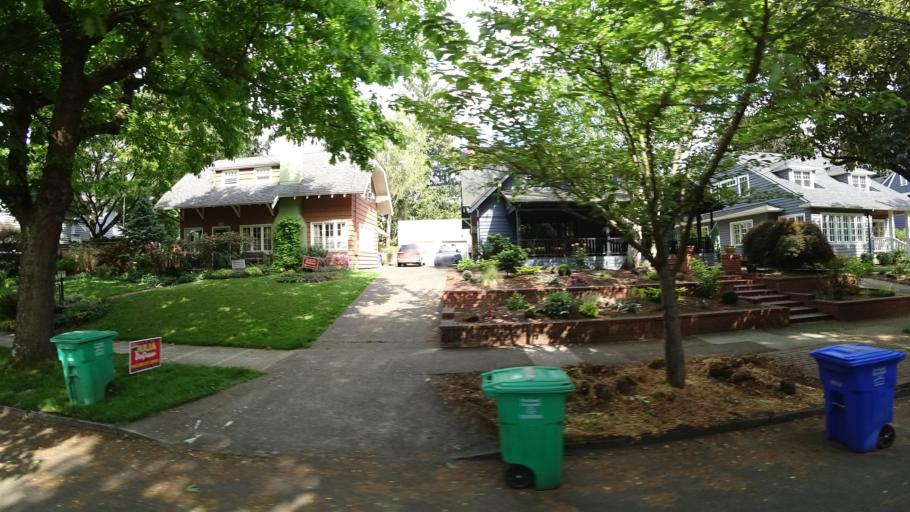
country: US
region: Oregon
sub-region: Multnomah County
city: Portland
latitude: 45.5461
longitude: -122.6463
